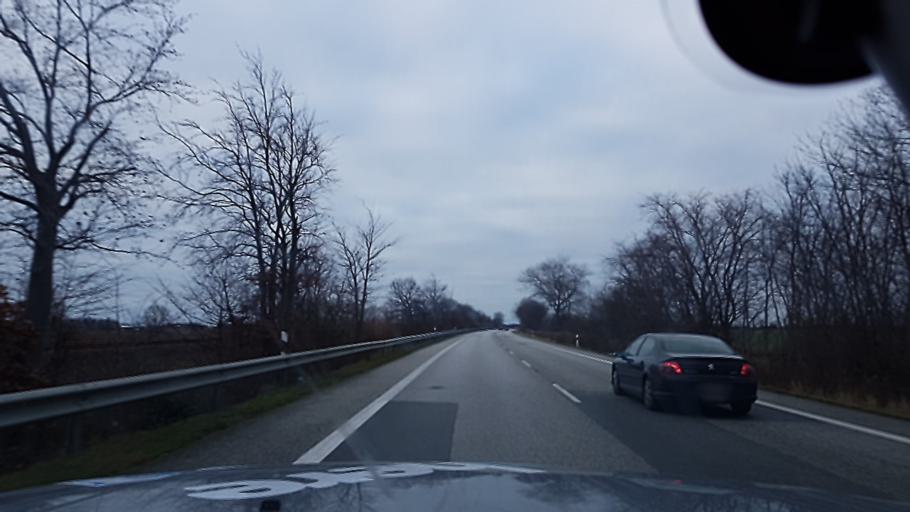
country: DE
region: Schleswig-Holstein
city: Fehmarn
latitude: 54.4587
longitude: 11.1934
